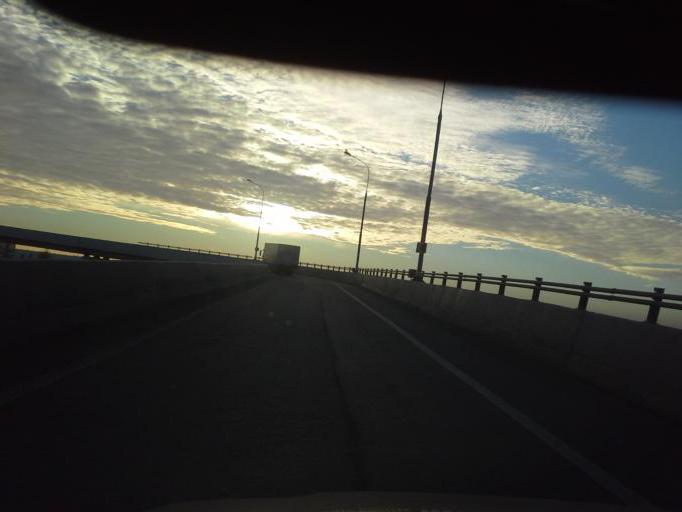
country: RU
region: Moscow
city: Vnukovo
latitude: 55.5868
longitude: 37.2124
